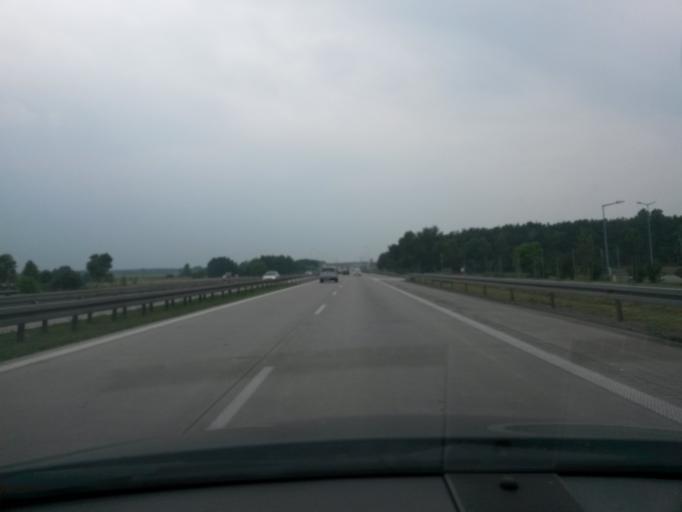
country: PL
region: Lodz Voivodeship
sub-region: Powiat piotrkowski
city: Wolborz
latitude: 51.5147
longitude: 19.9066
